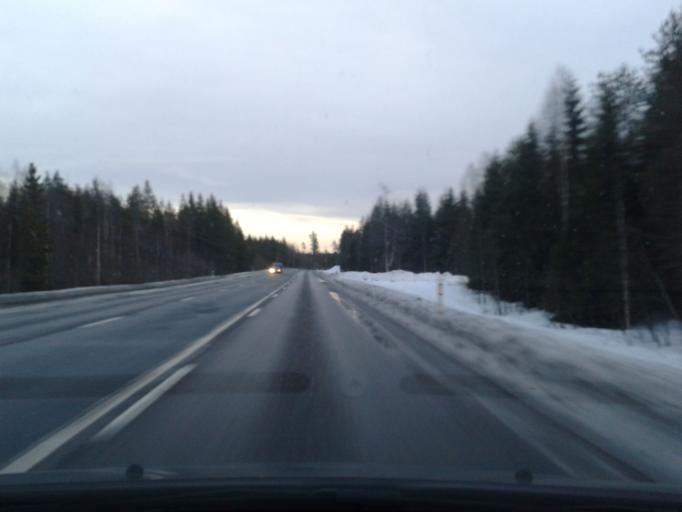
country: SE
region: Vaesternorrland
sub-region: Kramfors Kommun
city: Bollstabruk
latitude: 63.1077
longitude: 17.5057
